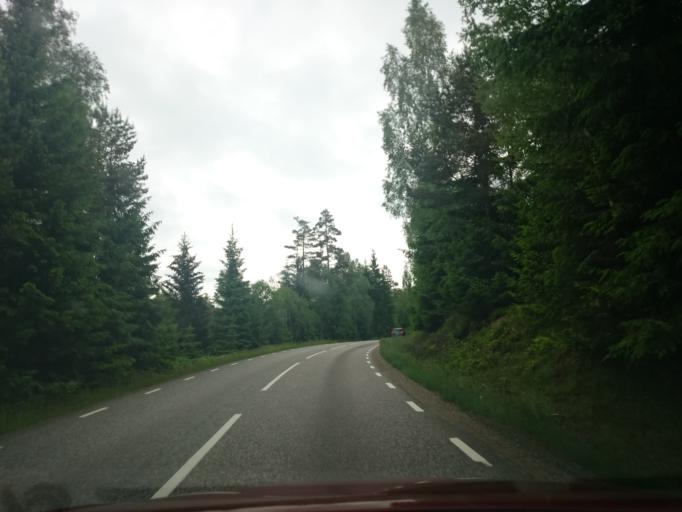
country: SE
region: Vaestra Goetaland
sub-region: Lerums Kommun
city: Stenkullen
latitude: 57.7088
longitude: 12.3515
